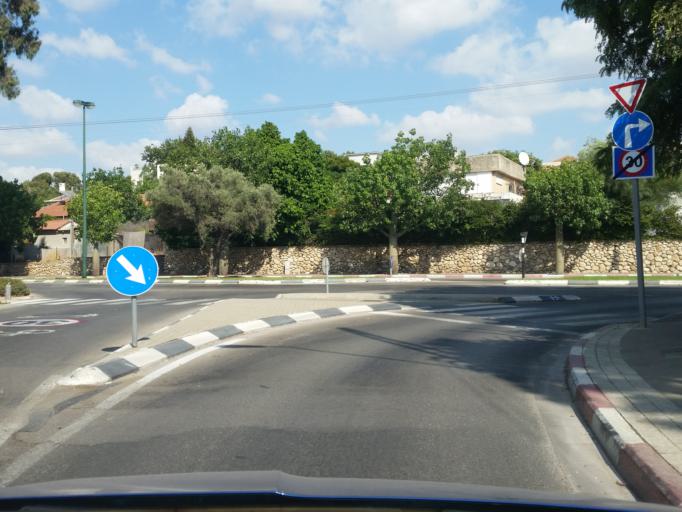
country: IL
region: Tel Aviv
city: Ramat HaSharon
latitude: 32.1154
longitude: 34.8329
